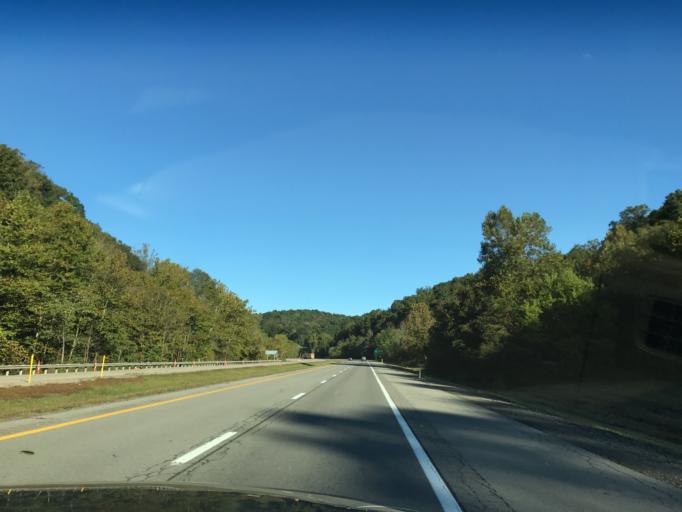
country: US
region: Ohio
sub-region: Washington County
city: Newport
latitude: 39.2429
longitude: -81.2295
